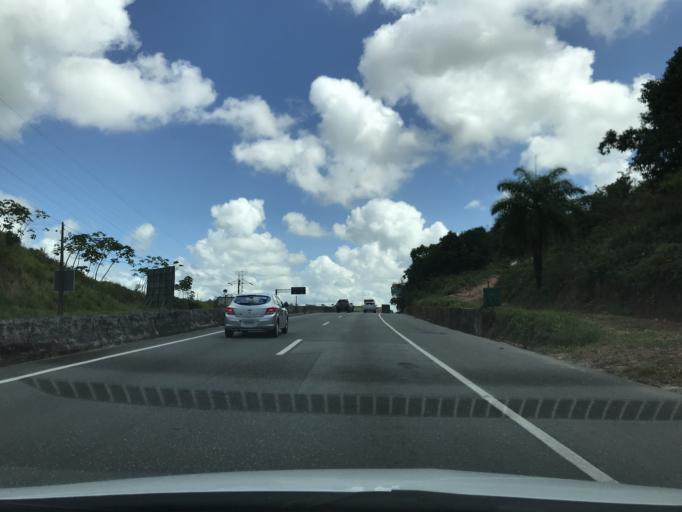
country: BR
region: Pernambuco
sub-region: Jaboatao Dos Guararapes
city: Jaboatao dos Guararapes
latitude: -8.0847
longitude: -34.9999
